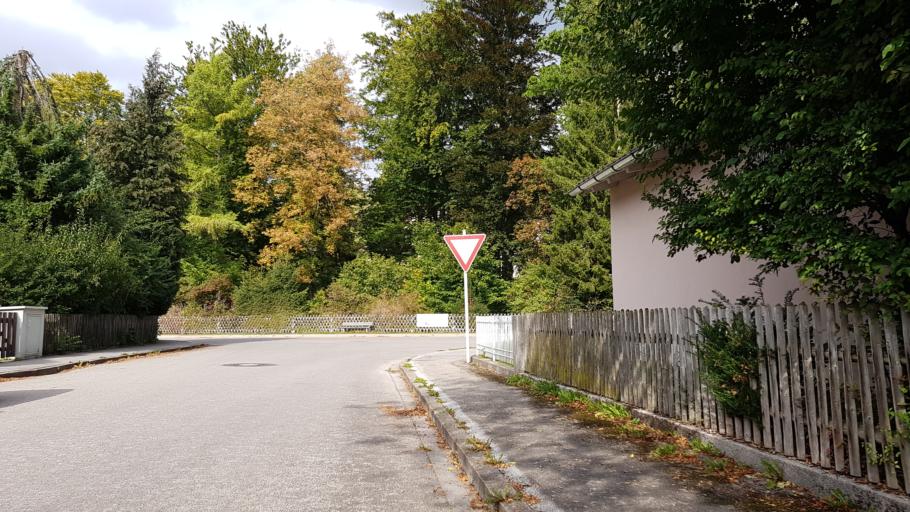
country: DE
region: Bavaria
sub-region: Swabia
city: Fuessen
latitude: 47.5717
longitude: 10.6883
